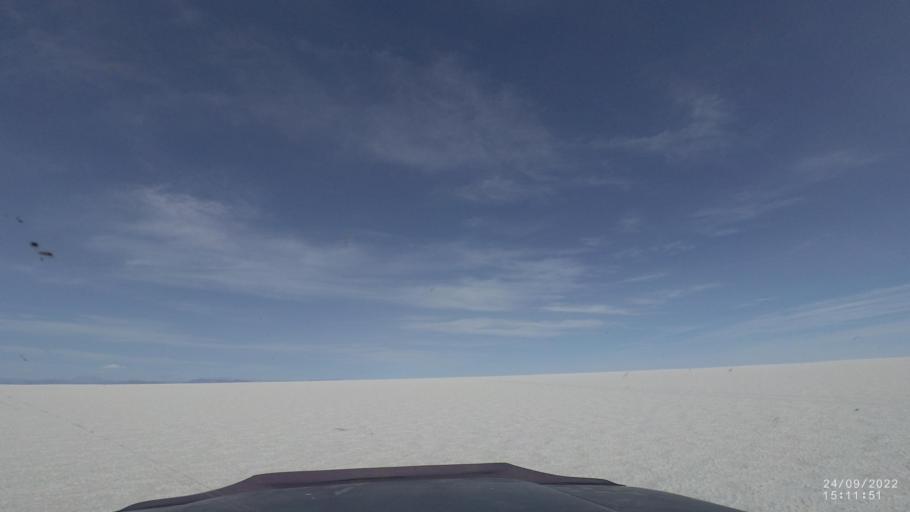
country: BO
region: Potosi
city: Colchani
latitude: -19.9469
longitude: -67.4745
